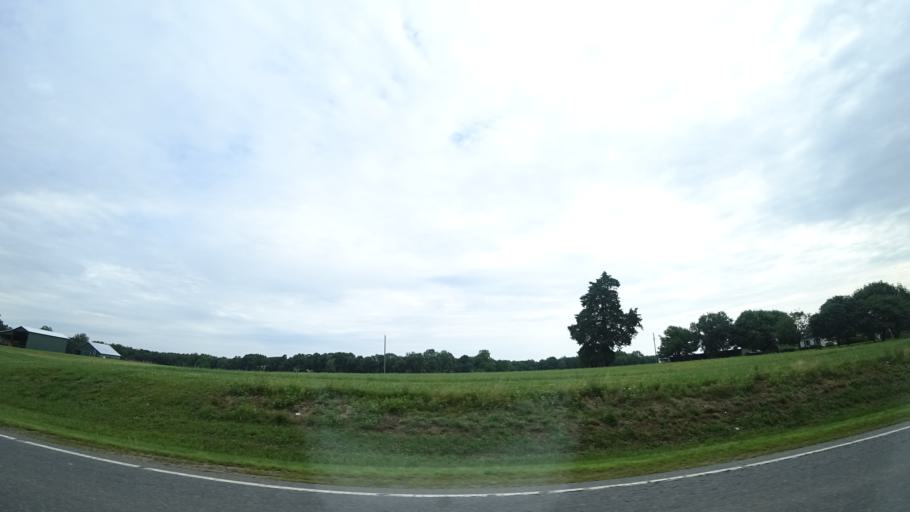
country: US
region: Virginia
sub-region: Spotsylvania County
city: Spotsylvania
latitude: 38.1479
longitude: -77.7059
